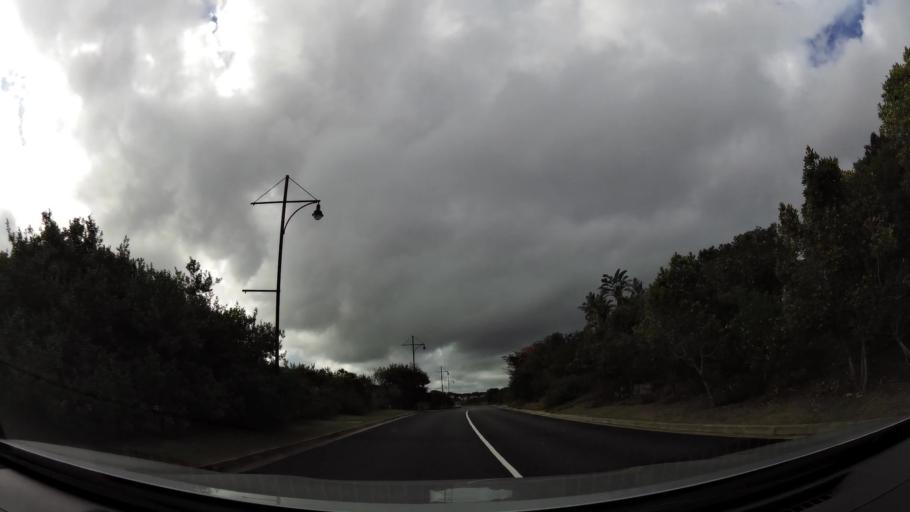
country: ZA
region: Western Cape
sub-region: Eden District Municipality
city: Knysna
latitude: -34.0691
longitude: 23.0899
